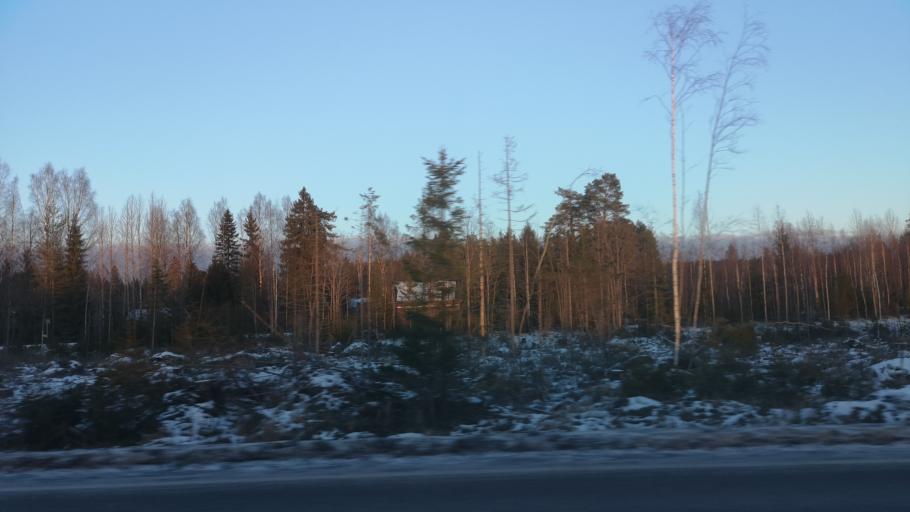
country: FI
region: Southern Savonia
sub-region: Savonlinna
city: Sulkava
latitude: 61.9478
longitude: 28.4996
